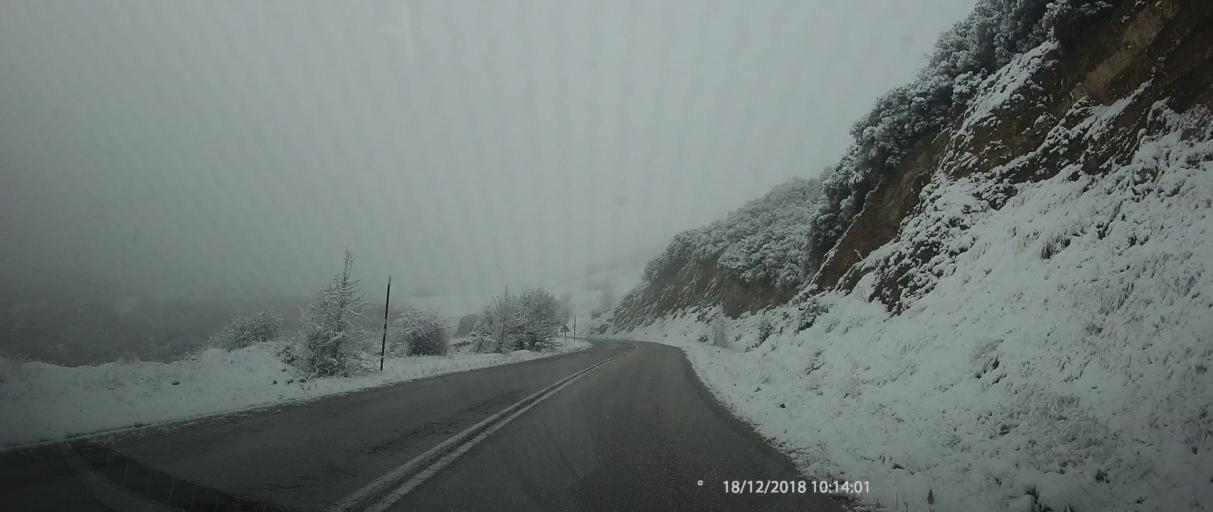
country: GR
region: Thessaly
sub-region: Nomos Larisis
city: Livadi
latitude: 40.1061
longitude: 22.2059
